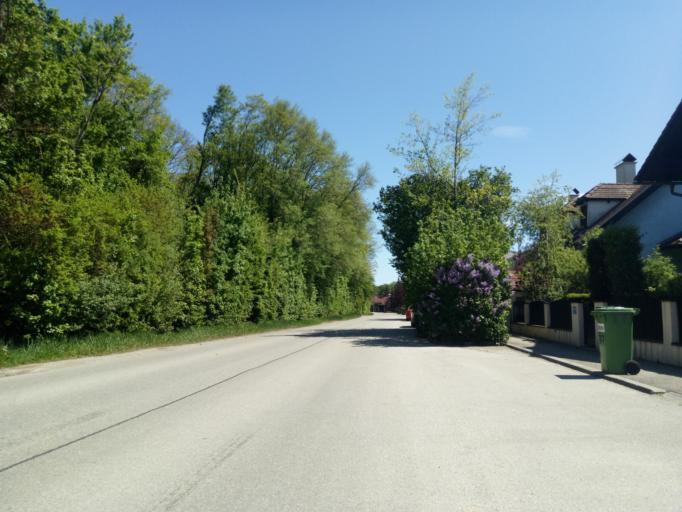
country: AT
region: Lower Austria
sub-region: Politischer Bezirk Modling
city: Kaltenleutgeben
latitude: 48.1304
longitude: 16.1897
